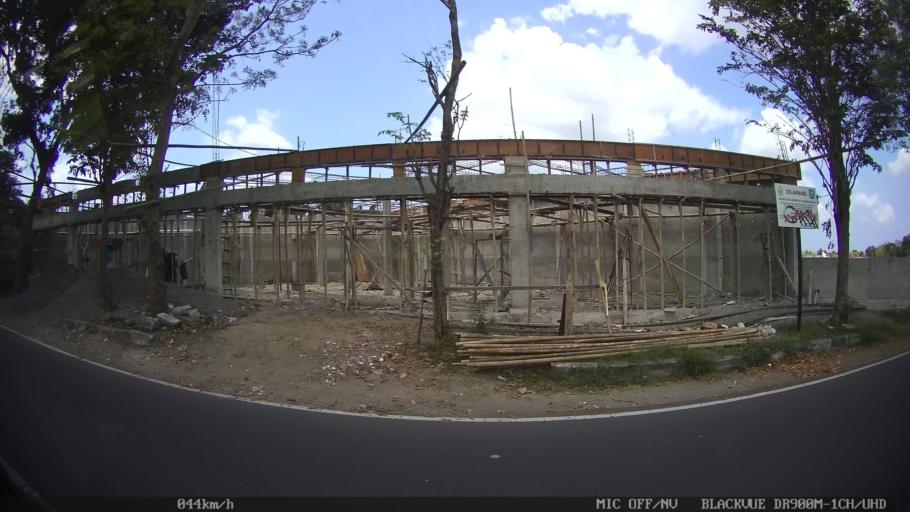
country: ID
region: Daerah Istimewa Yogyakarta
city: Bantul
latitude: -7.8806
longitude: 110.3361
